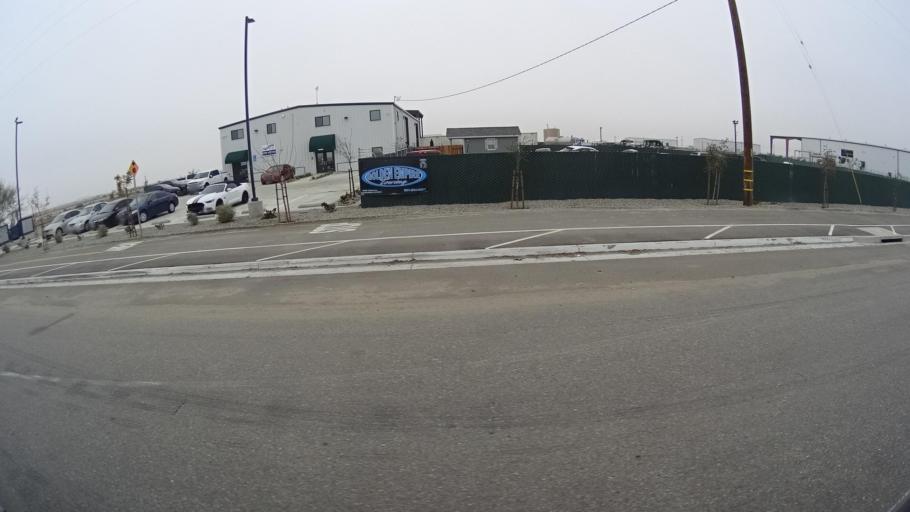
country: US
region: California
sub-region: Kern County
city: Rosedale
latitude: 35.2616
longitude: -119.2528
